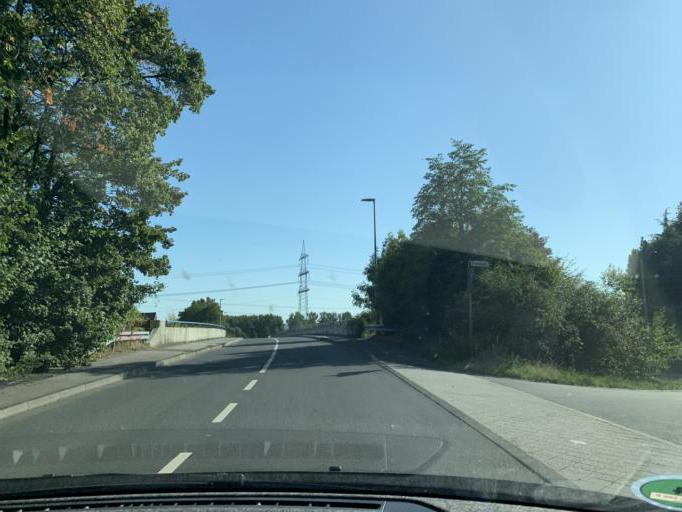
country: DE
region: North Rhine-Westphalia
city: Schwerte
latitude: 51.4614
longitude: 7.5748
